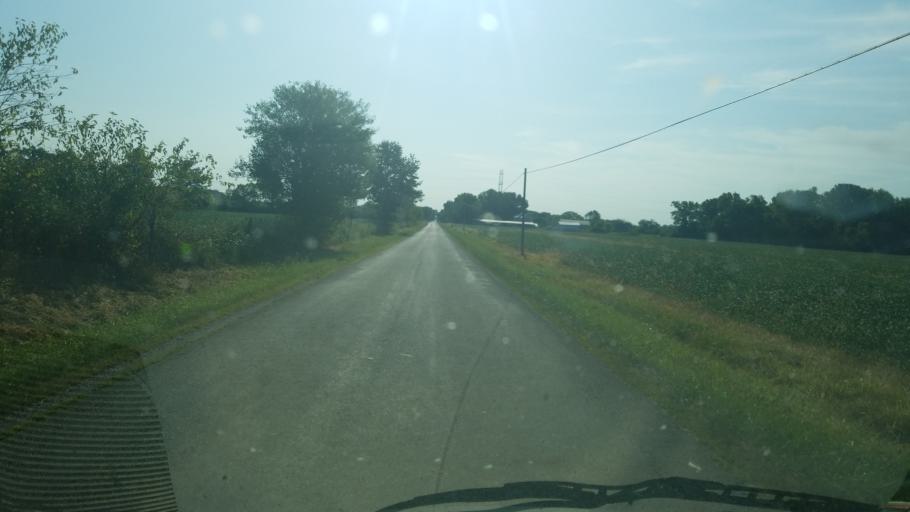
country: US
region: Ohio
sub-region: Franklin County
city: Lake Darby
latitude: 39.8921
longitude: -83.1816
